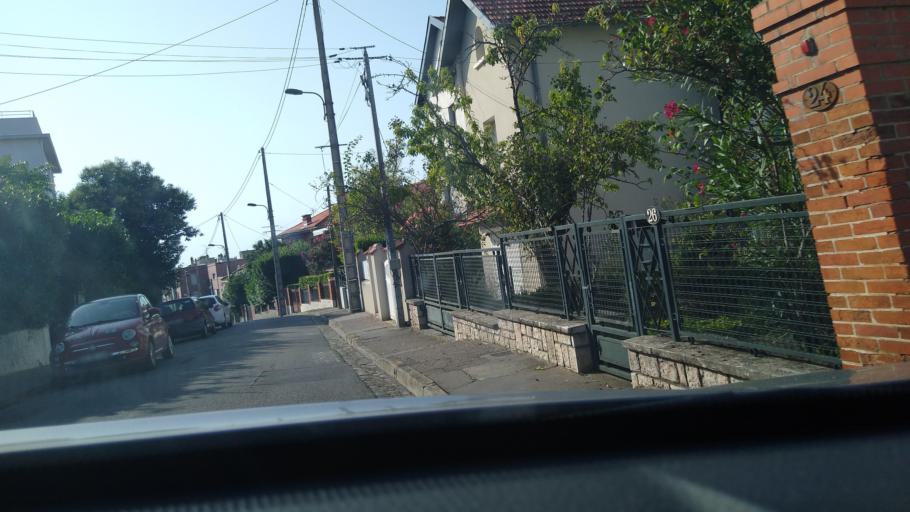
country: FR
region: Midi-Pyrenees
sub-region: Departement de la Haute-Garonne
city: Toulouse
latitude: 43.6189
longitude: 1.4592
